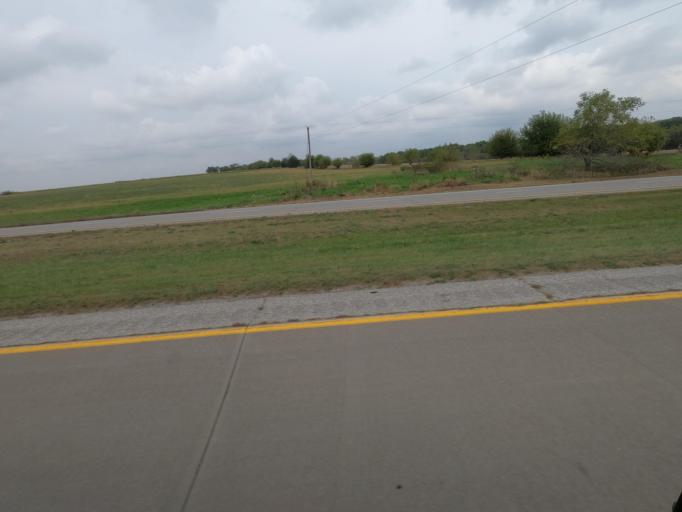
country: US
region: Iowa
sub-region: Wapello County
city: Eddyville
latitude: 41.1210
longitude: -92.5573
